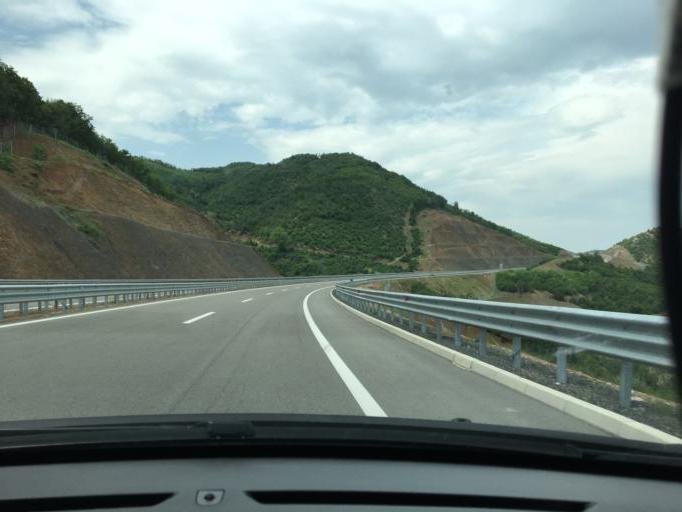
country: MK
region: Gevgelija
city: Miravci
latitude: 41.3523
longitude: 22.3624
